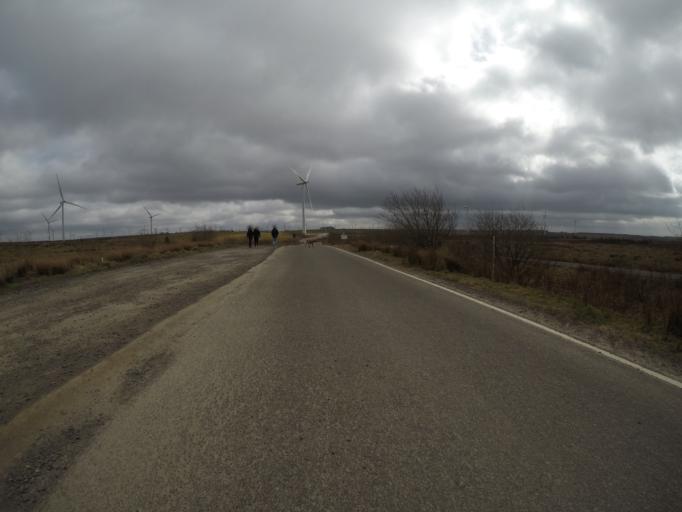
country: GB
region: Scotland
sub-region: East Renfrewshire
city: Newton Mearns
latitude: 55.7030
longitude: -4.3552
